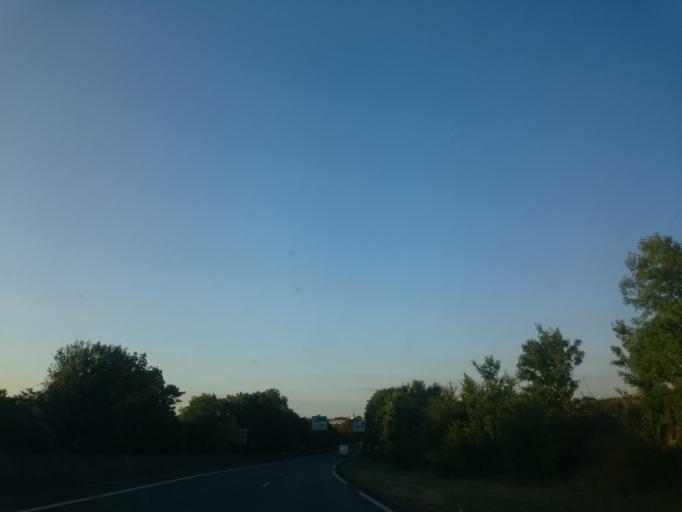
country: FR
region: Ile-de-France
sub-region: Departement de l'Essonne
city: Etampes
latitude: 48.4150
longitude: 2.1299
